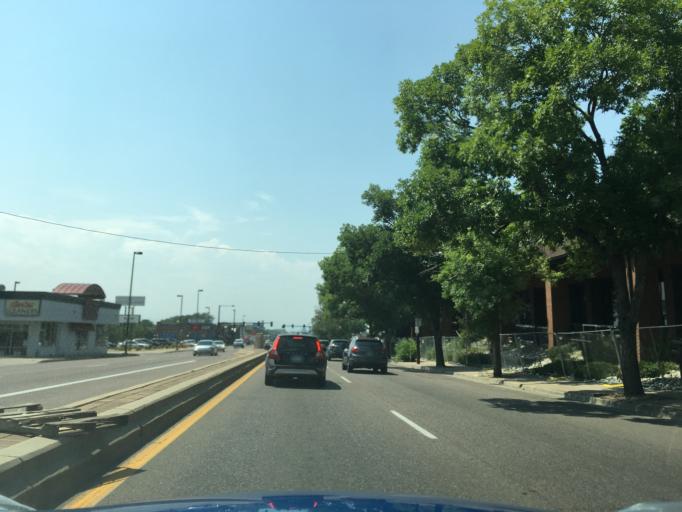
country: US
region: Colorado
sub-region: Arapahoe County
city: Glendale
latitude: 39.7402
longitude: -104.9140
